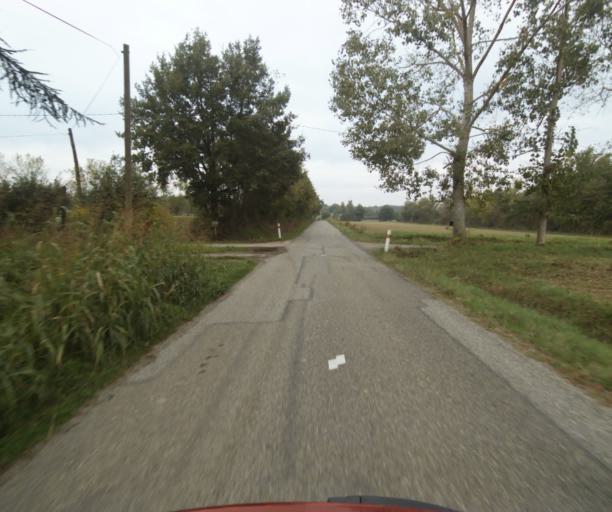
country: FR
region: Midi-Pyrenees
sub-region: Departement du Tarn-et-Garonne
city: Verdun-sur-Garonne
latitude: 43.8336
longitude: 1.1922
